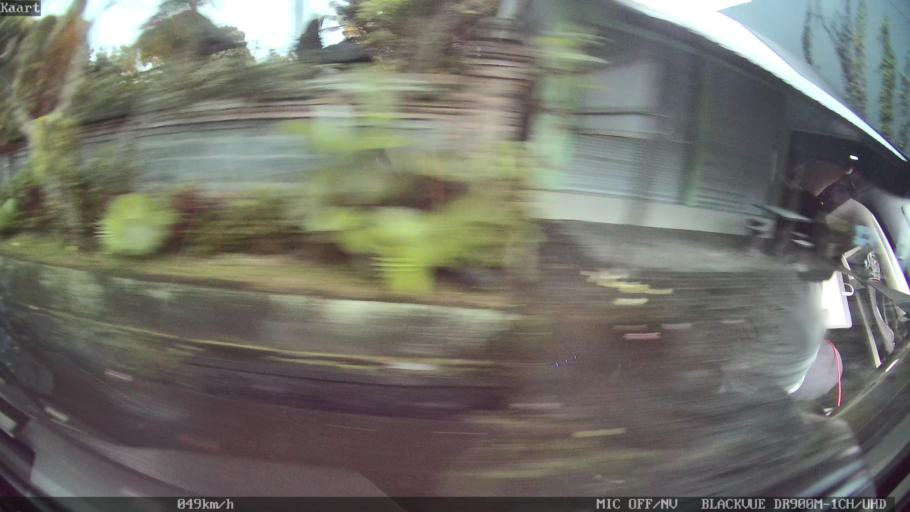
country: ID
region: Bali
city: Banjar Teguan
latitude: -8.5090
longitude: 115.2299
